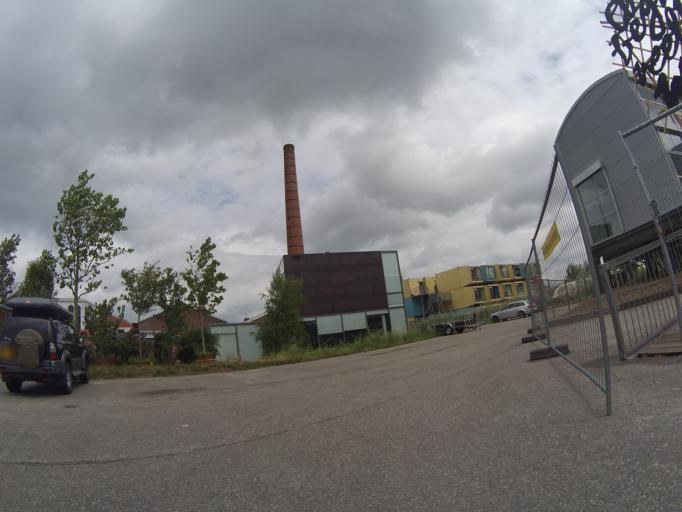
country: NL
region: Utrecht
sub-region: Gemeente Amersfoort
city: Amersfoort
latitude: 52.1607
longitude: 5.3803
